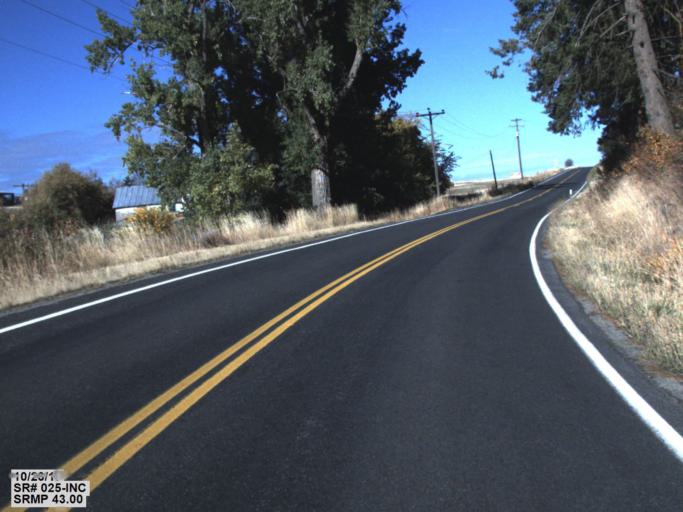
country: US
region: Washington
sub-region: Lincoln County
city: Davenport
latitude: 48.1249
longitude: -118.2090
